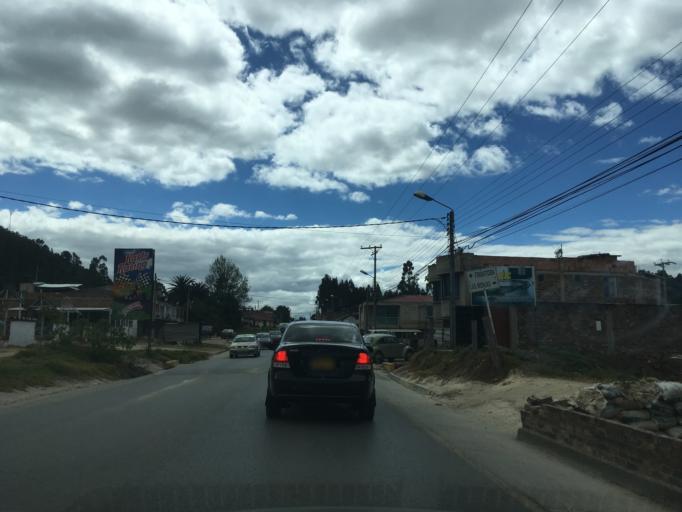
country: CO
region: Boyaca
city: Sogamoso
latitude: 5.6950
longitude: -72.9422
